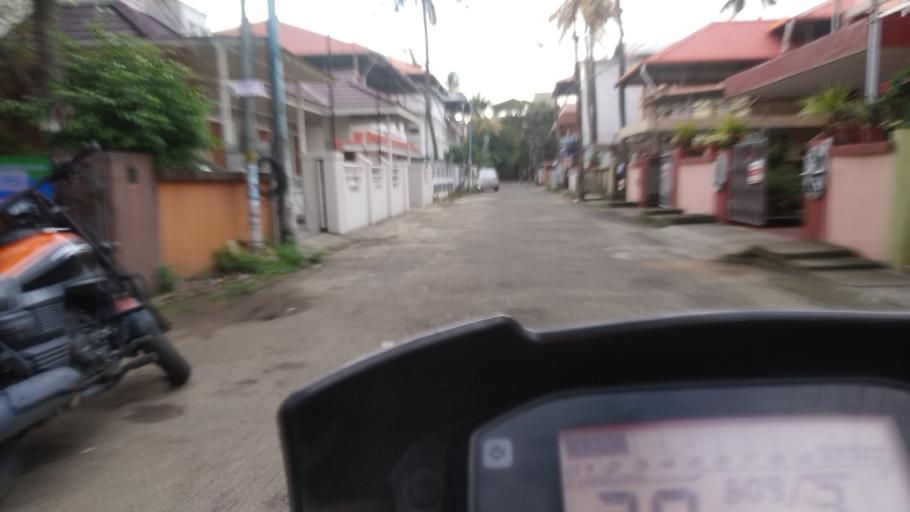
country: IN
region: Kerala
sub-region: Ernakulam
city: Cochin
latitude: 9.9630
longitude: 76.2983
